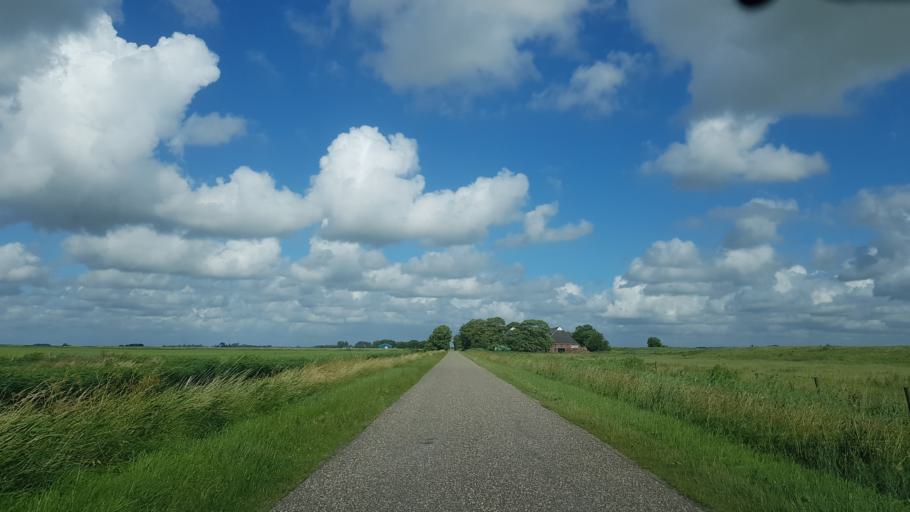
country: NL
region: Groningen
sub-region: Gemeente Winsum
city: Winsum
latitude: 53.4065
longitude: 6.5451
